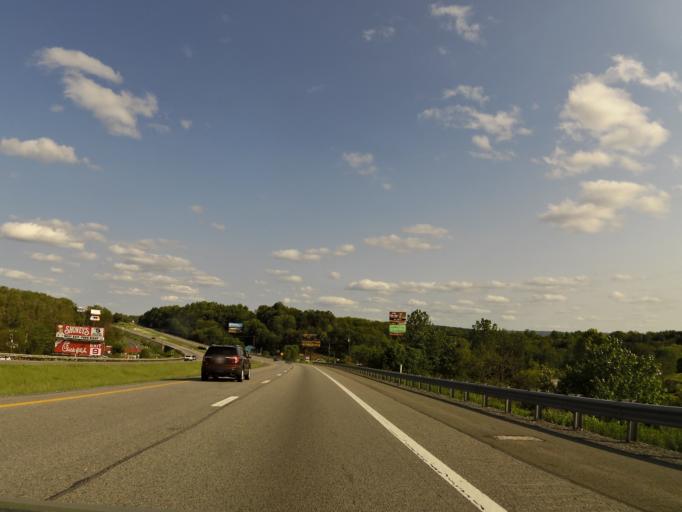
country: US
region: West Virginia
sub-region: Mercer County
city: Princeton
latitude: 37.3897
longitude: -81.0578
